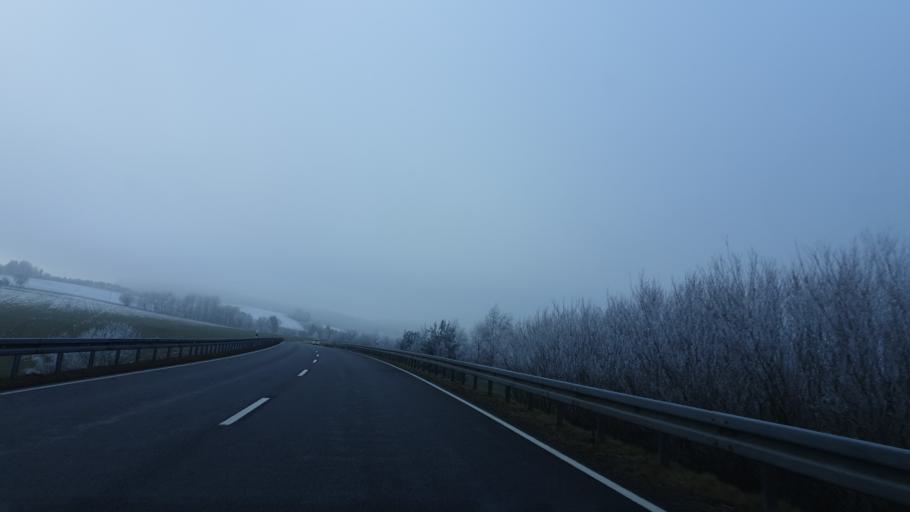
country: DE
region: Saxony
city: Bad Brambach
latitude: 50.2308
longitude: 12.3143
